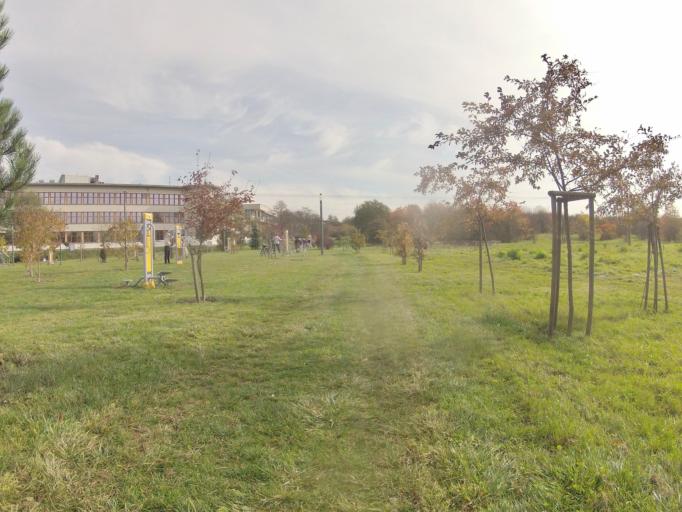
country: PL
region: Lesser Poland Voivodeship
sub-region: Krakow
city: Sidzina
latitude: 50.0261
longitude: 19.8988
